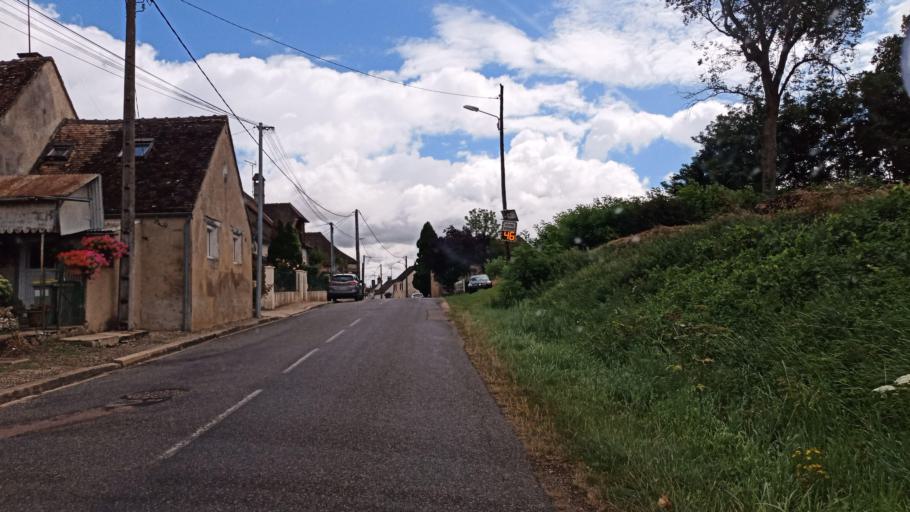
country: FR
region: Bourgogne
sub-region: Departement de l'Yonne
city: Cheroy
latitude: 48.2416
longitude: 3.0421
